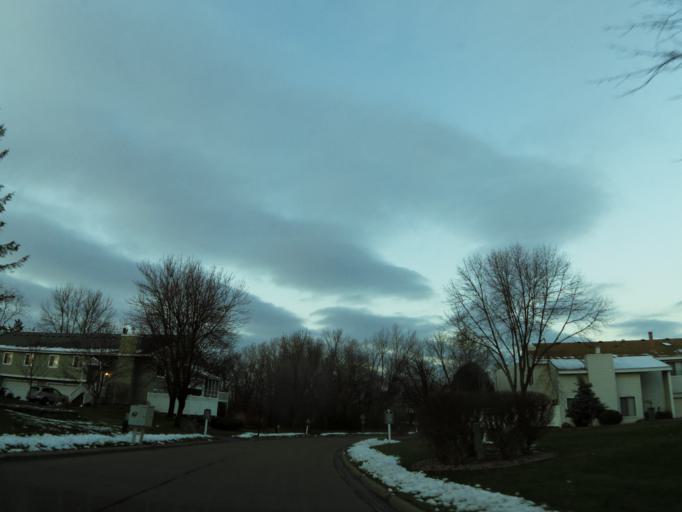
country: US
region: Minnesota
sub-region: Hennepin County
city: Minnetonka Mills
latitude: 44.9033
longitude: -93.4261
